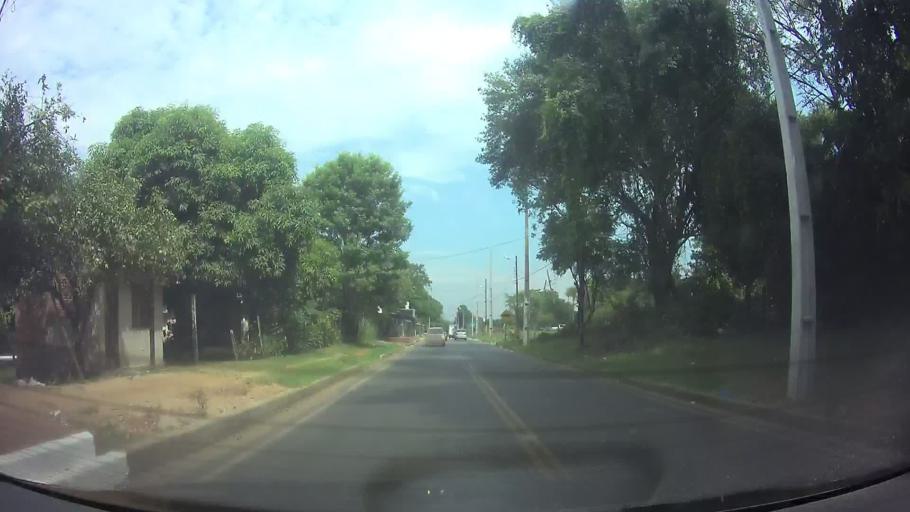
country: PY
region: Central
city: Fernando de la Mora
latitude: -25.2972
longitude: -57.5334
